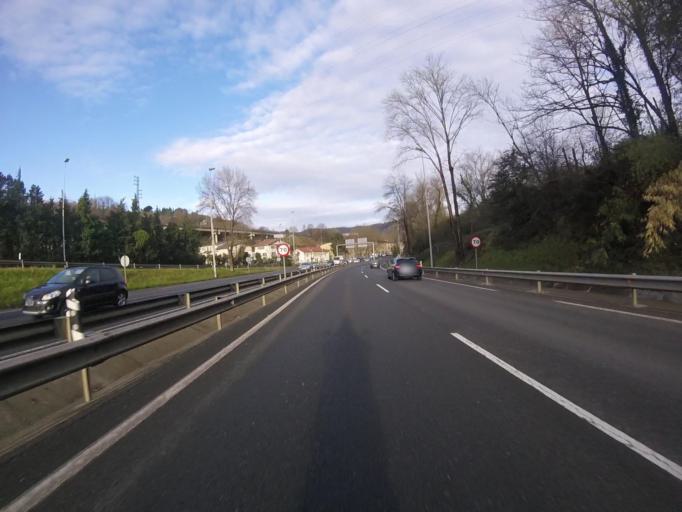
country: ES
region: Basque Country
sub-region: Provincia de Guipuzcoa
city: San Sebastian
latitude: 43.2974
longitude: -1.9983
